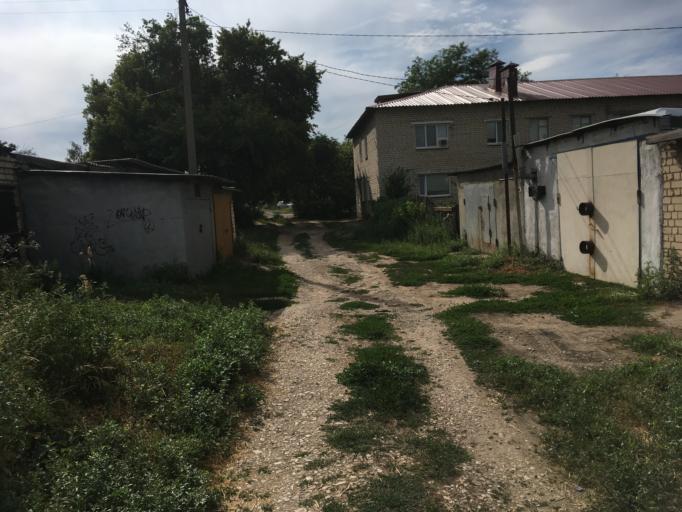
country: RU
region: Samara
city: Bezenchuk
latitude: 52.9874
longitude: 49.4430
